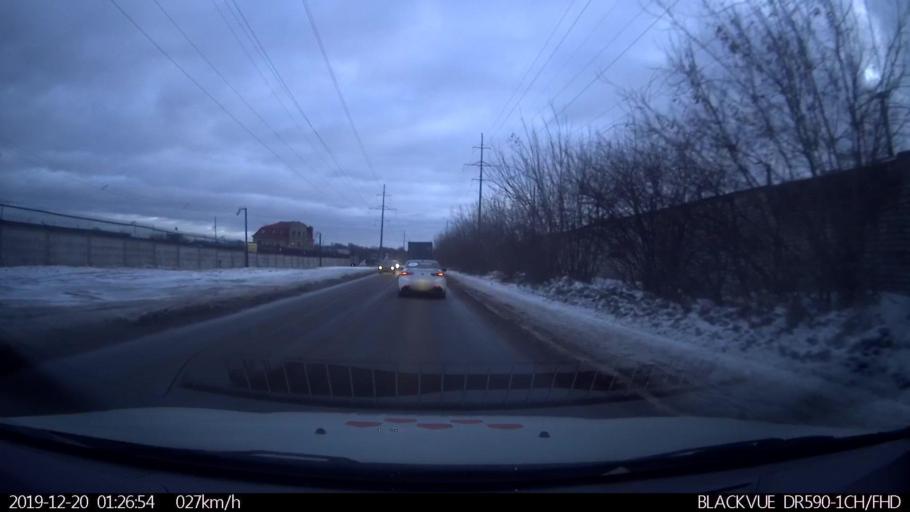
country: RU
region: Nizjnij Novgorod
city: Nizhniy Novgorod
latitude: 56.3040
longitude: 44.0086
